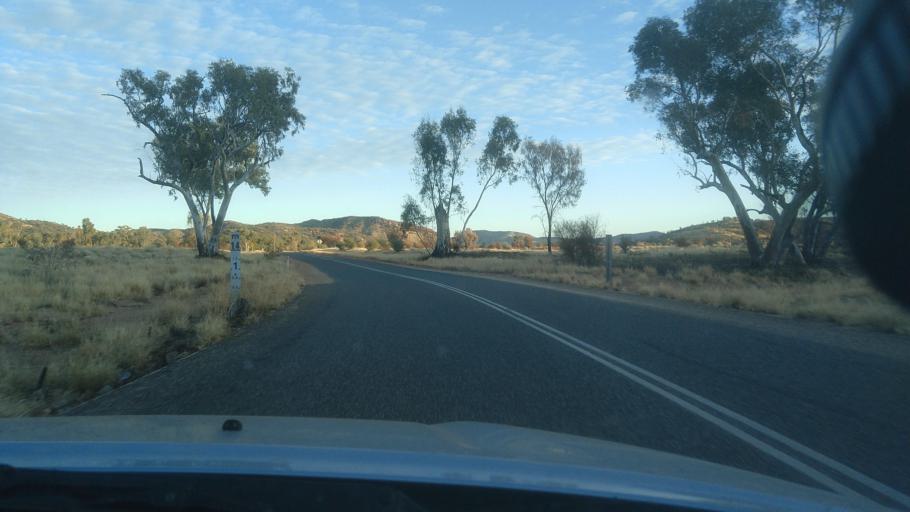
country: AU
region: Northern Territory
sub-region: Alice Springs
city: Alice Springs
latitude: -23.7361
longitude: 133.7417
